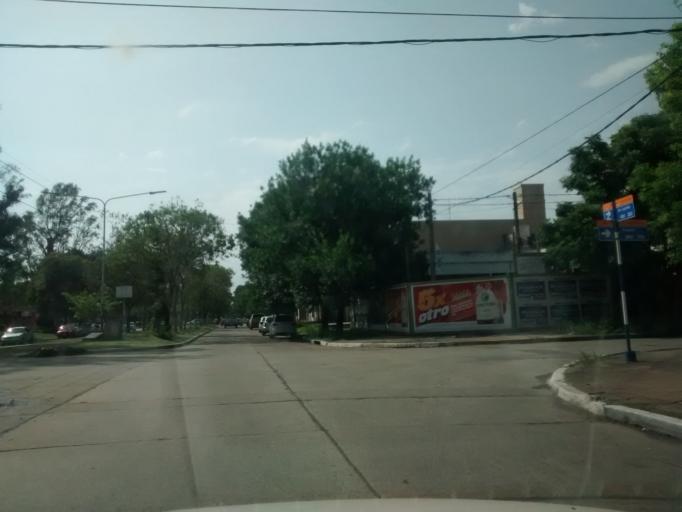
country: AR
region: Chaco
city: Resistencia
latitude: -27.4479
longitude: -58.9762
